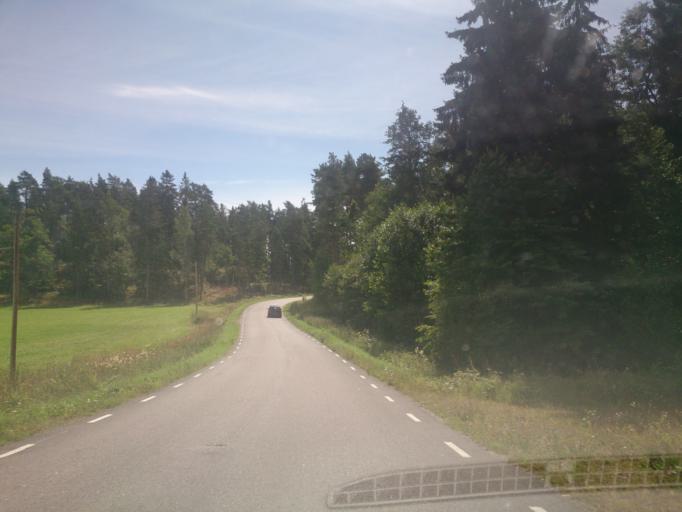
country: SE
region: OEstergoetland
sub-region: Valdemarsviks Kommun
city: Valdemarsvik
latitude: 58.3231
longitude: 16.6457
